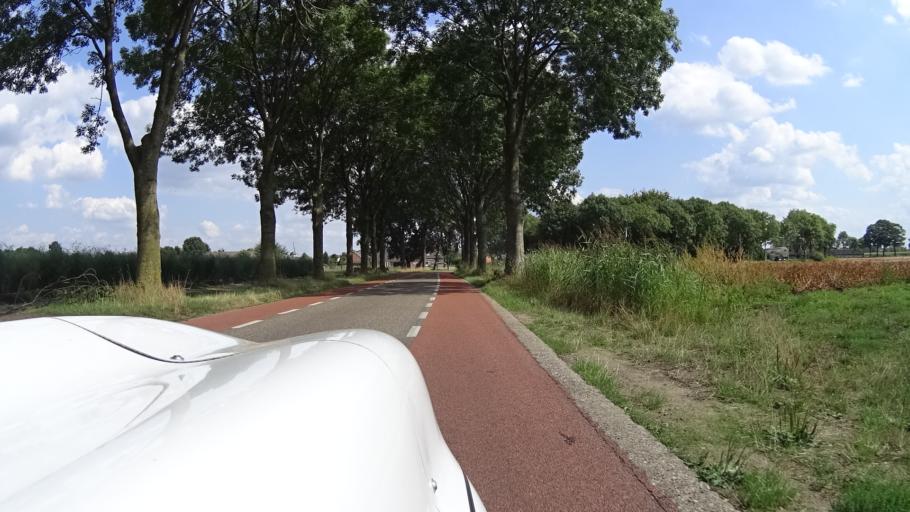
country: NL
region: North Brabant
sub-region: Gemeente Veghel
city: Veghel
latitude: 51.6521
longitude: 5.5424
